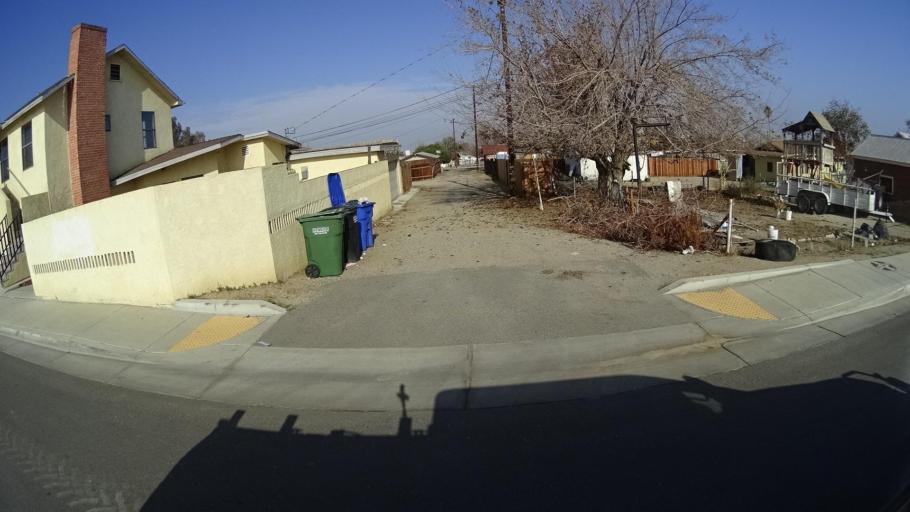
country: US
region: California
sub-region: Kern County
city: South Taft
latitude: 35.1367
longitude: -119.4640
